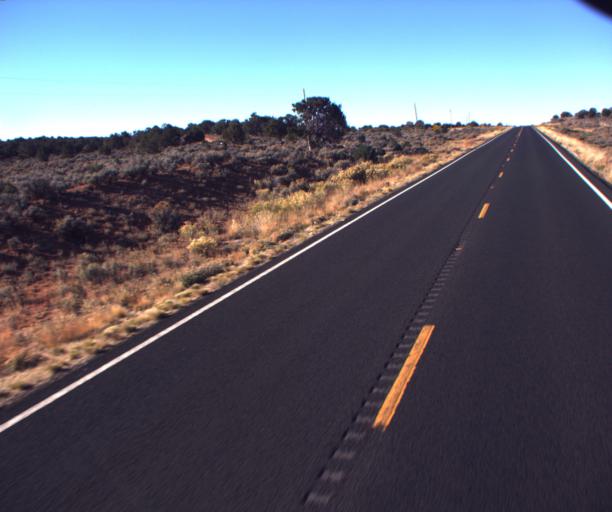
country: US
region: Arizona
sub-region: Apache County
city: Ganado
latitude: 35.7683
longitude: -109.7443
